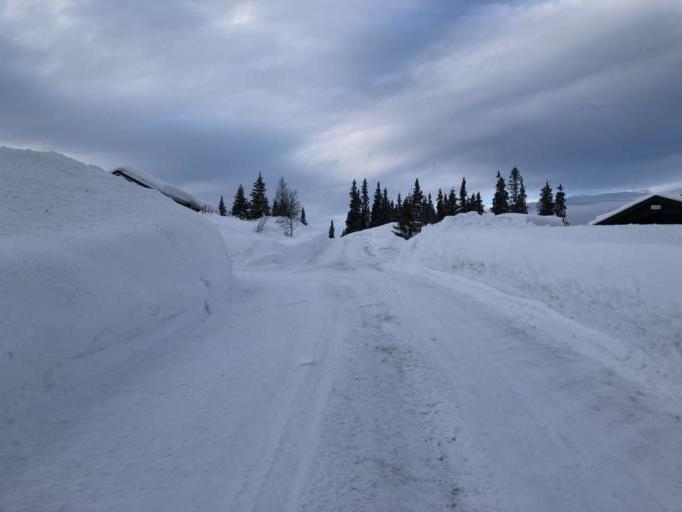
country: NO
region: Oppland
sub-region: Gausdal
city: Segalstad bru
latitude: 61.3294
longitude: 10.0534
